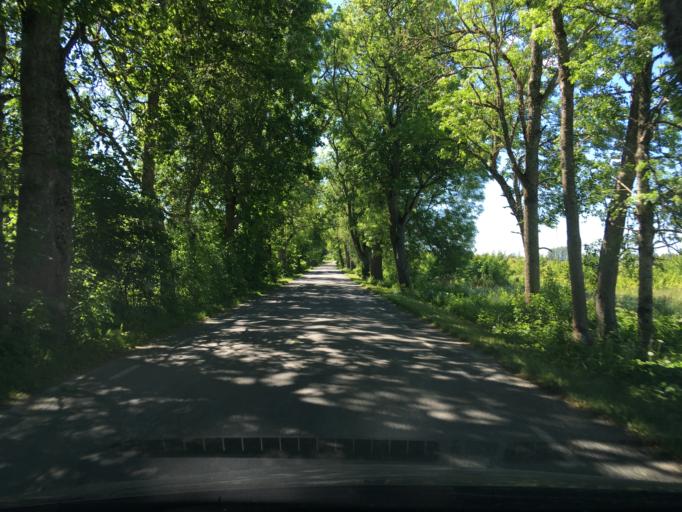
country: EE
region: Raplamaa
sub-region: Kohila vald
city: Kohila
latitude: 59.1034
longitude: 24.8170
